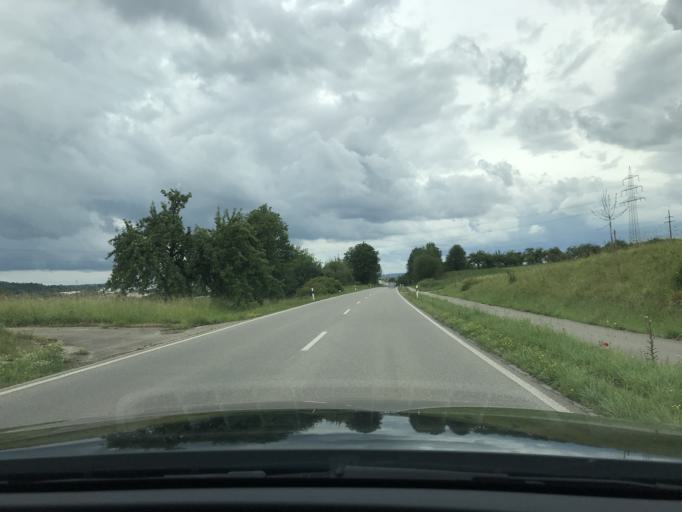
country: DE
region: Baden-Wuerttemberg
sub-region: Regierungsbezirk Stuttgart
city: Schwaikheim
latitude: 48.8886
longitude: 9.3606
